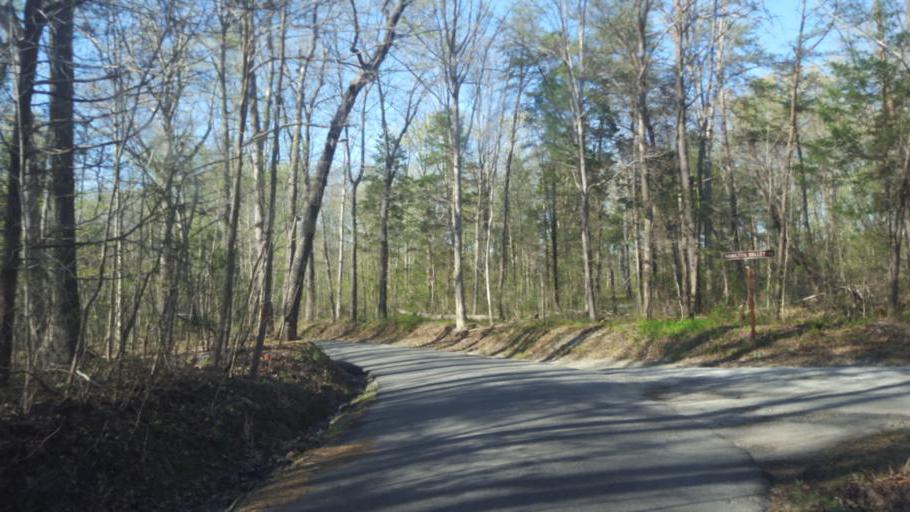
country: US
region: Kentucky
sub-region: Barren County
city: Cave City
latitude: 37.1862
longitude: -86.0480
